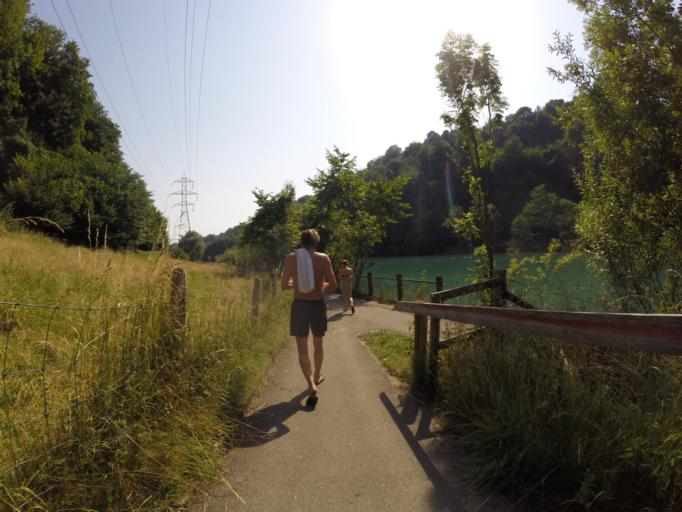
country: CH
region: Bern
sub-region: Bern-Mittelland District
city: Bern
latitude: 46.9648
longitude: 7.4451
